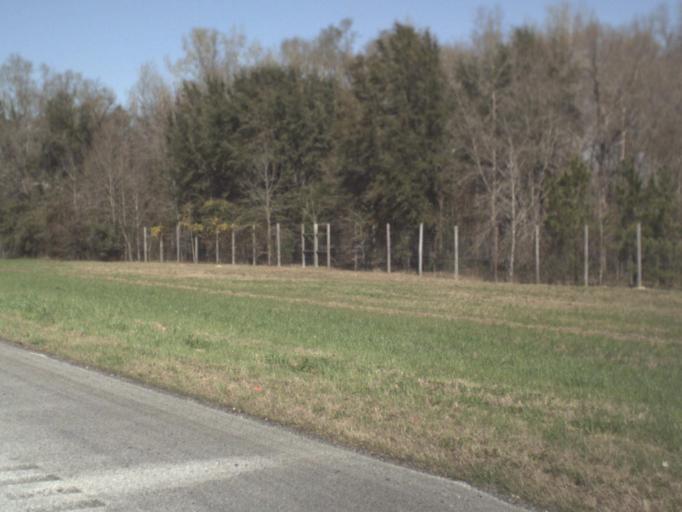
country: US
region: Florida
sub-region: Jackson County
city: Marianna
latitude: 30.6841
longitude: -85.1036
